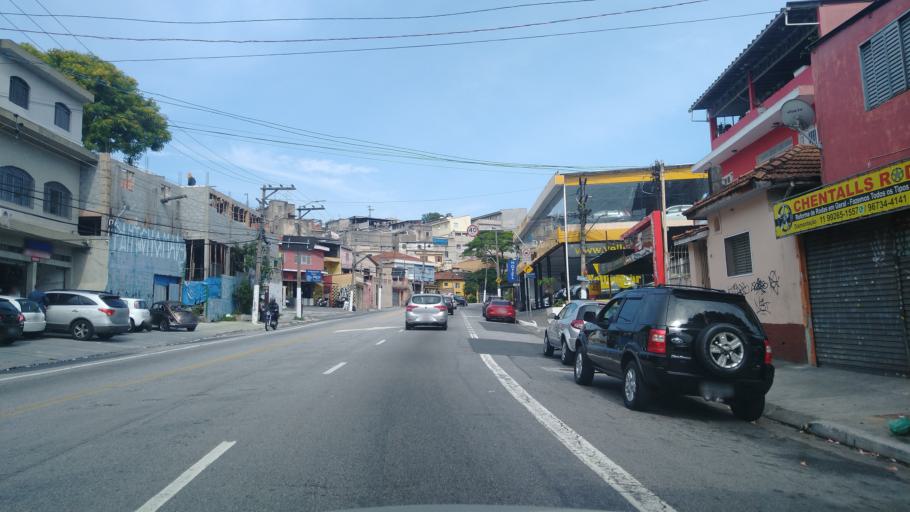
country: BR
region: Sao Paulo
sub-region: Sao Paulo
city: Sao Paulo
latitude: -23.4800
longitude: -46.6607
